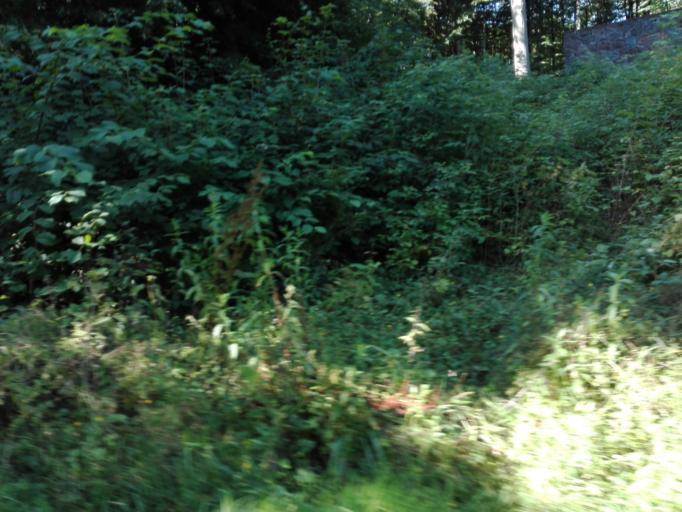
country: DK
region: Central Jutland
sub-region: Odder Kommune
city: Odder
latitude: 55.9656
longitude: 10.1221
